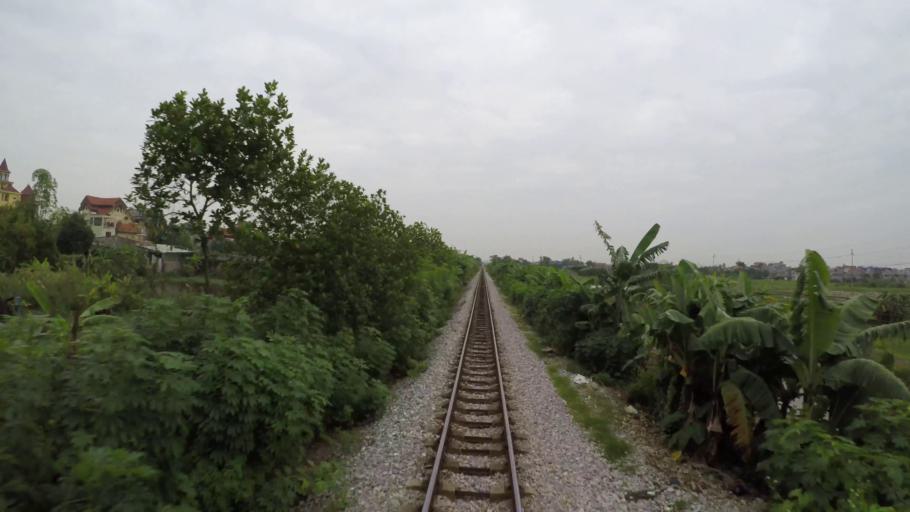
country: VN
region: Hai Phong
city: An Duong
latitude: 20.8934
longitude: 106.5895
